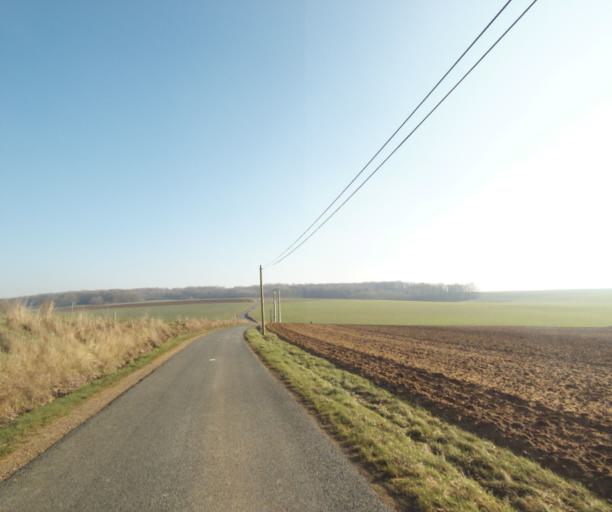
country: FR
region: Champagne-Ardenne
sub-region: Departement de la Haute-Marne
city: Wassy
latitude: 48.5105
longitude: 5.0161
